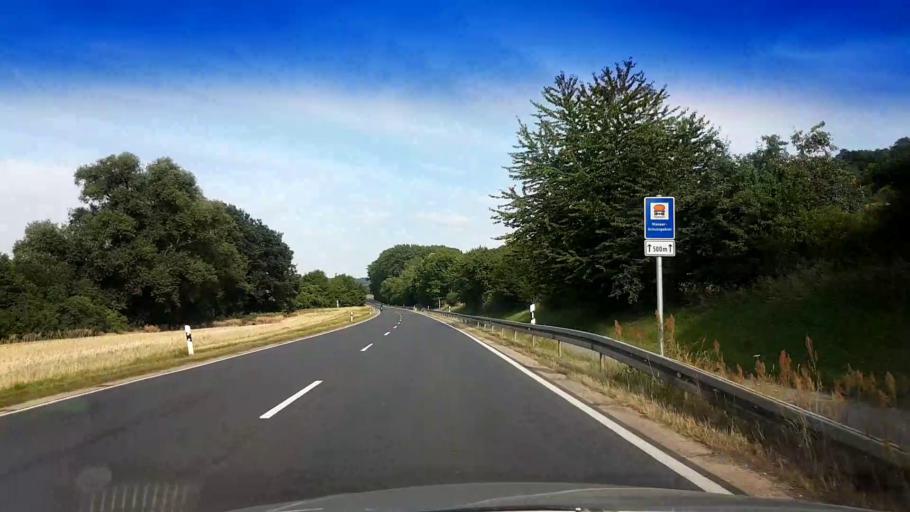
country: DE
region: Bavaria
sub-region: Regierungsbezirk Unterfranken
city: Eltmann
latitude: 49.9696
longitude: 10.6799
